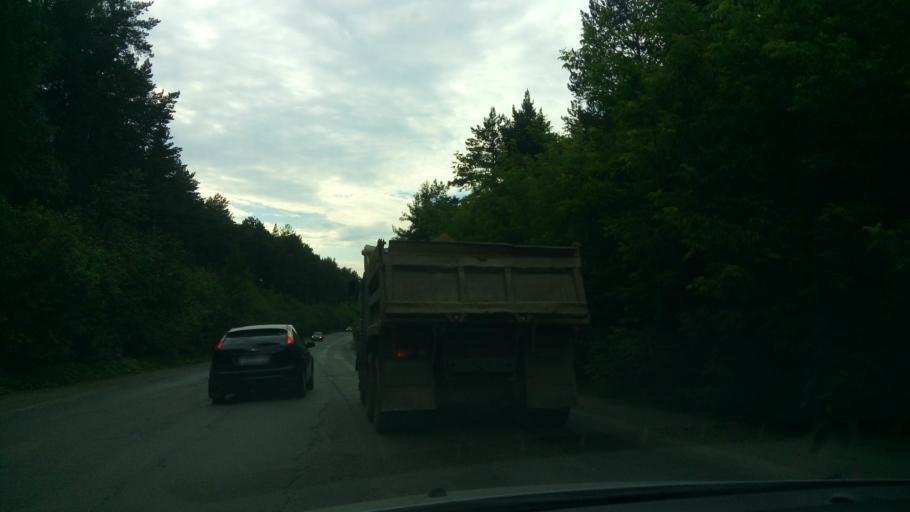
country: RU
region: Sverdlovsk
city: Yekaterinburg
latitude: 56.8862
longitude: 60.6779
